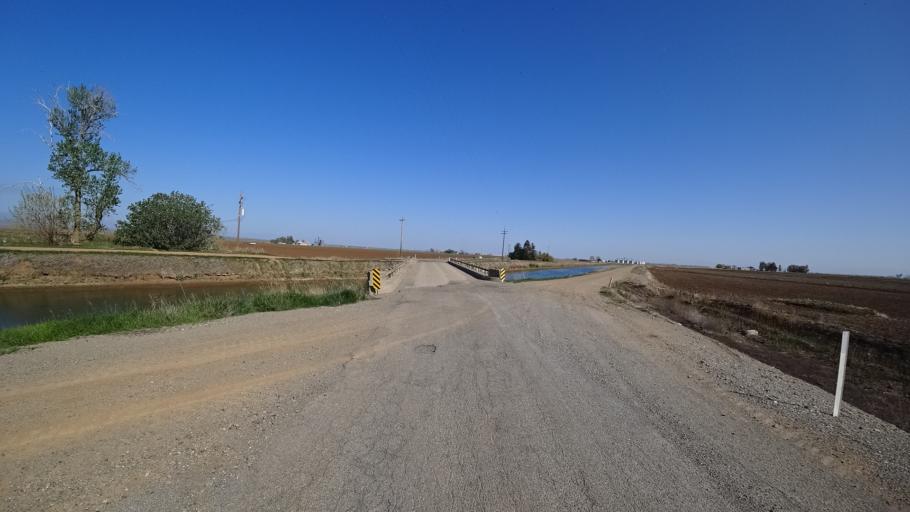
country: US
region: California
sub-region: Glenn County
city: Willows
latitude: 39.4418
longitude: -122.2303
